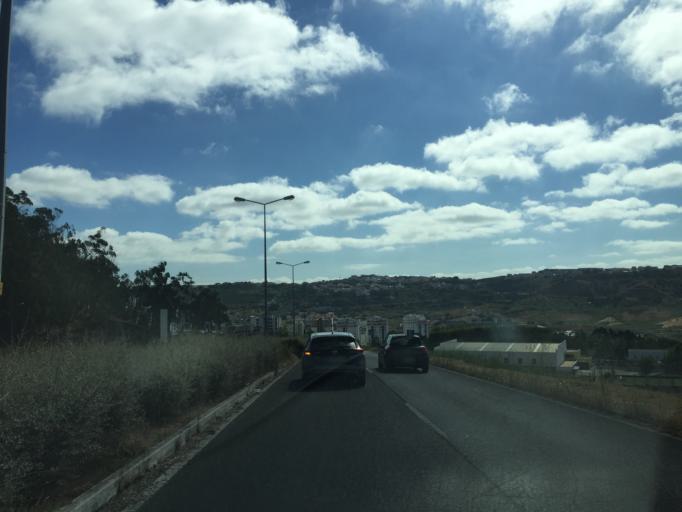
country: PT
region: Lisbon
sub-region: Odivelas
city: Povoa de Santo Adriao
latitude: 38.8071
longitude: -9.1668
